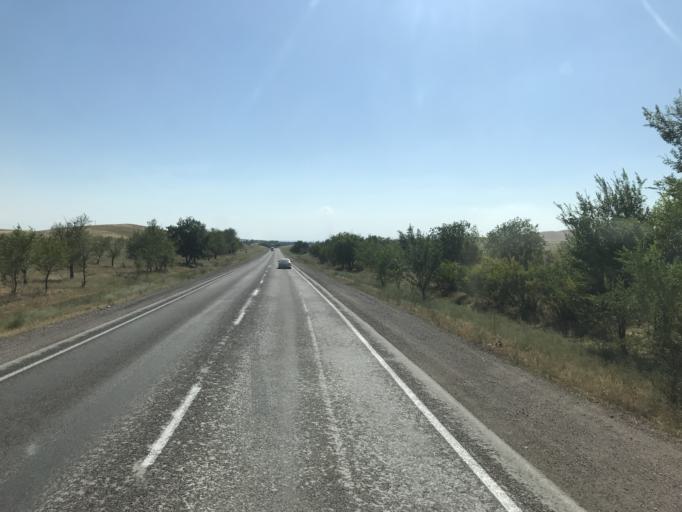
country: KZ
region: Zhambyl
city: Georgiyevka
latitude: 43.2468
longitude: 74.7900
